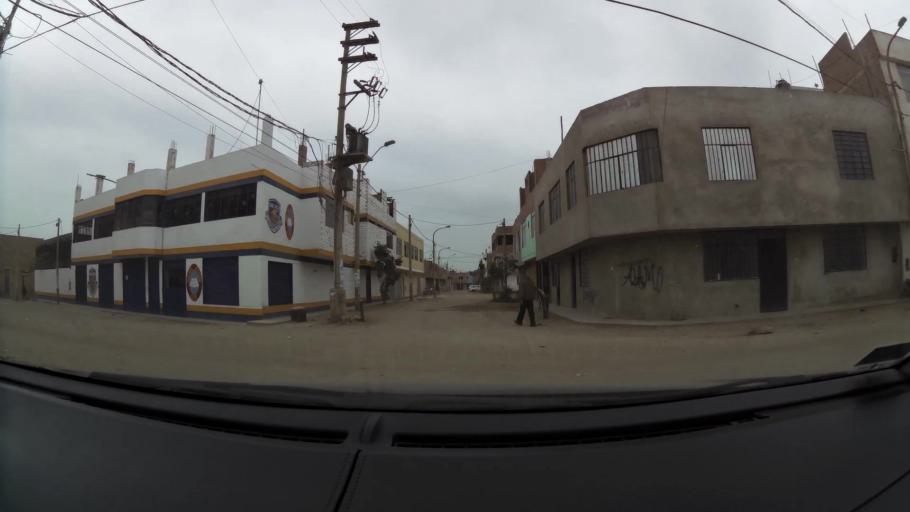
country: PE
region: Lima
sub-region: Lima
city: Independencia
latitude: -11.9627
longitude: -77.0952
